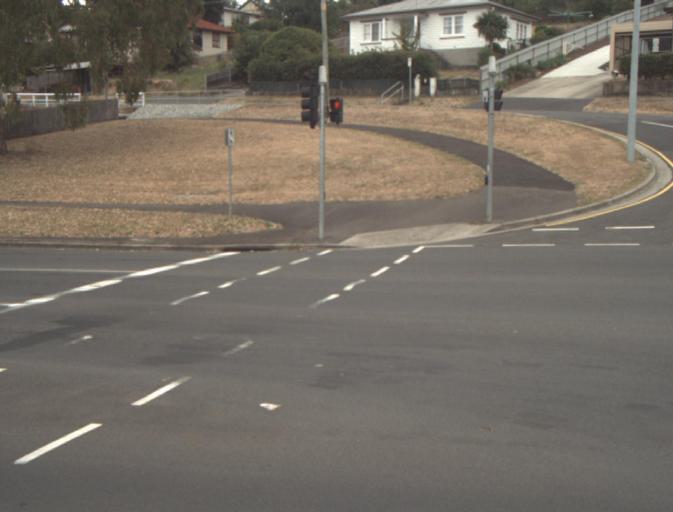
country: AU
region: Tasmania
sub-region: Launceston
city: Newnham
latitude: -41.4094
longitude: 147.1320
